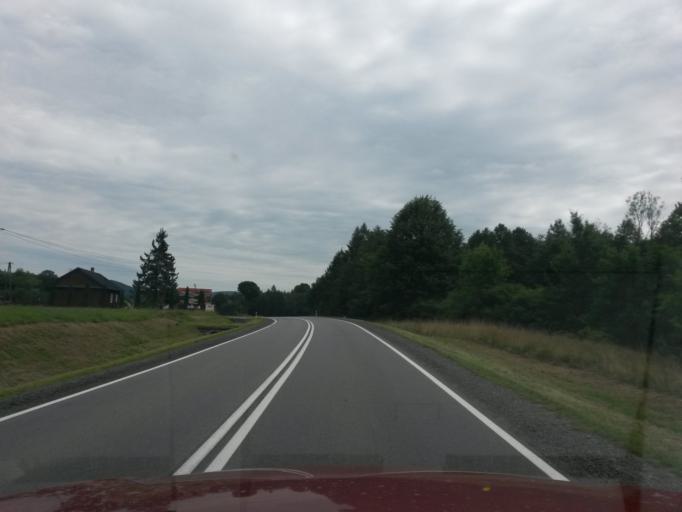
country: PL
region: Lesser Poland Voivodeship
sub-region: Powiat nowosadecki
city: Kamionka Wielka
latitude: 49.5360
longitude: 20.8155
